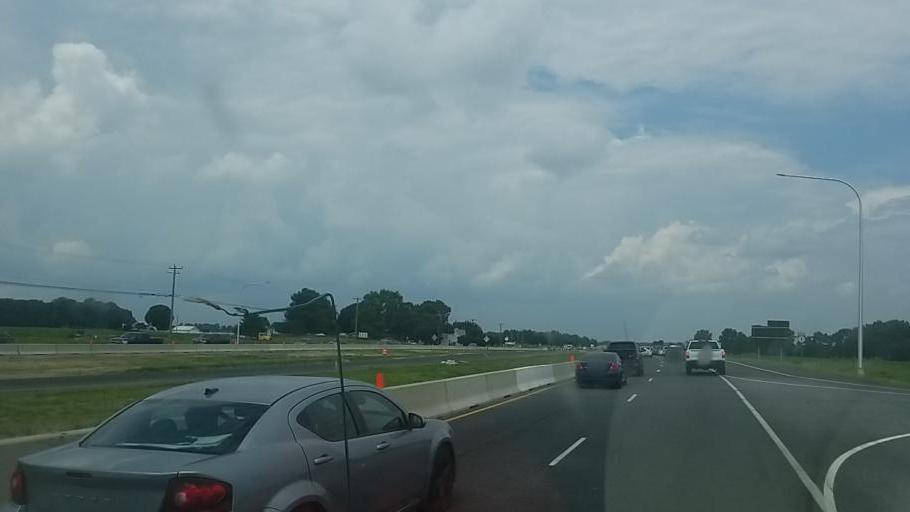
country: US
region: Delaware
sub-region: Kent County
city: Riverview
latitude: 39.0296
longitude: -75.4587
